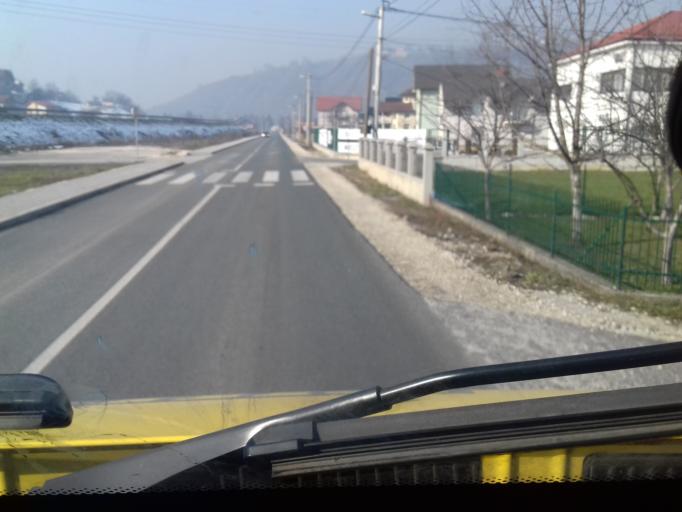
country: BA
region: Federation of Bosnia and Herzegovina
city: Ilijas
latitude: 43.9372
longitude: 18.2949
